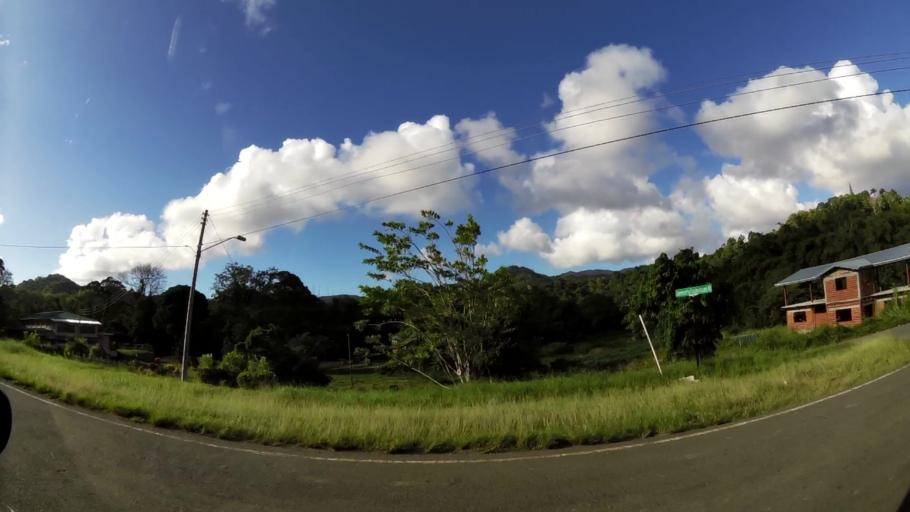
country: TT
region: Eastern Tobago
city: Roxborough
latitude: 11.2259
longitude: -60.6118
